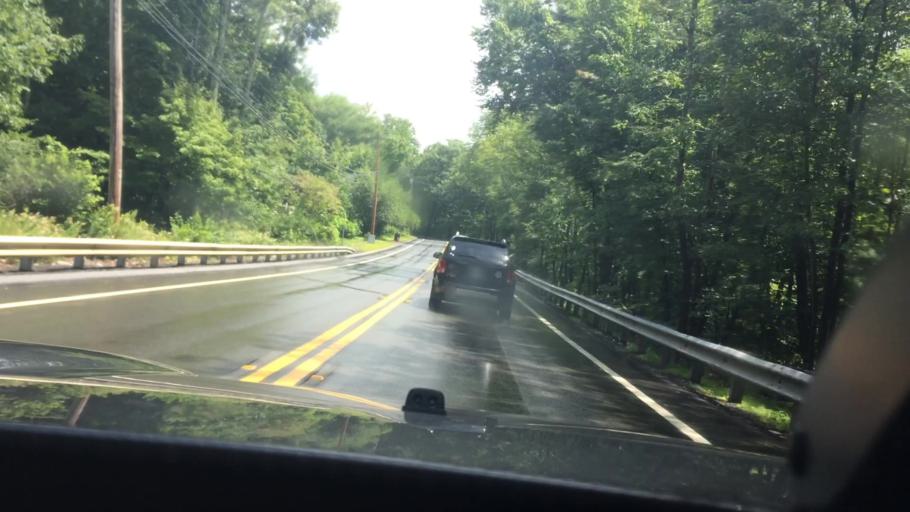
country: US
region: Massachusetts
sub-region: Worcester County
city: Phillipston
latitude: 42.5700
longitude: -72.1537
